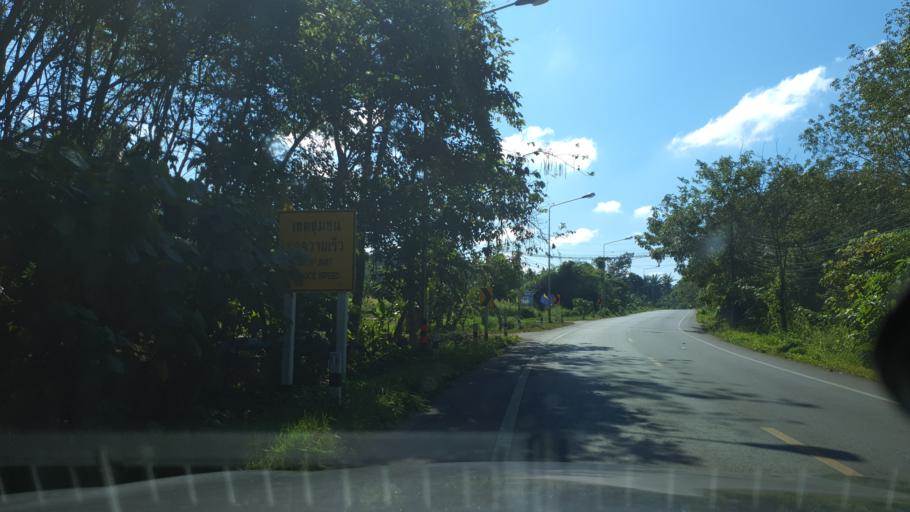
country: TH
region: Phangnga
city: Ban Ao Nang
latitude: 8.0740
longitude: 98.8065
